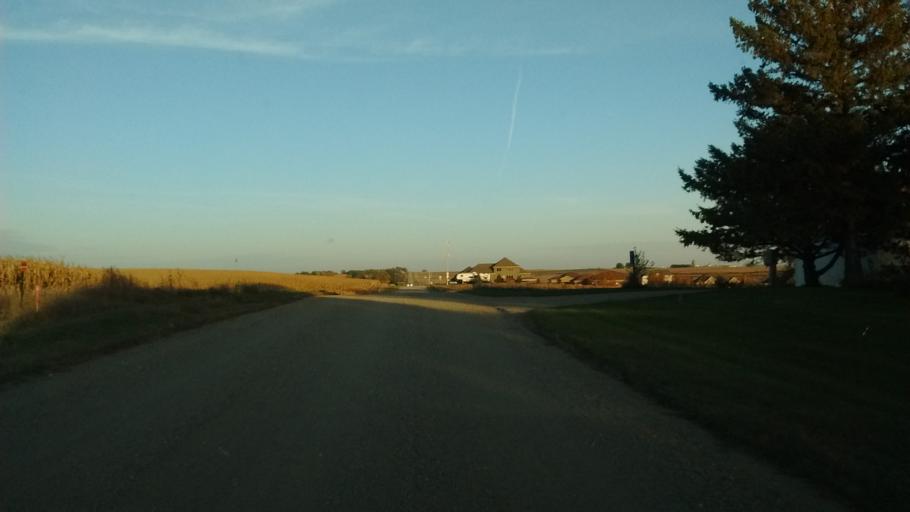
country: US
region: Iowa
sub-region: Plymouth County
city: Le Mars
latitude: 42.7642
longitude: -96.1636
